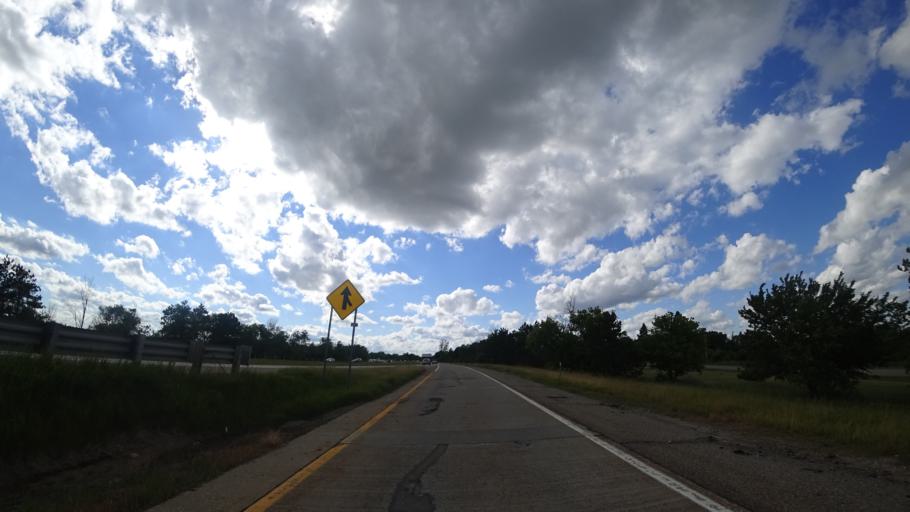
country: US
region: Michigan
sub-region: Ionia County
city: Portland
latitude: 42.8747
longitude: -84.9659
